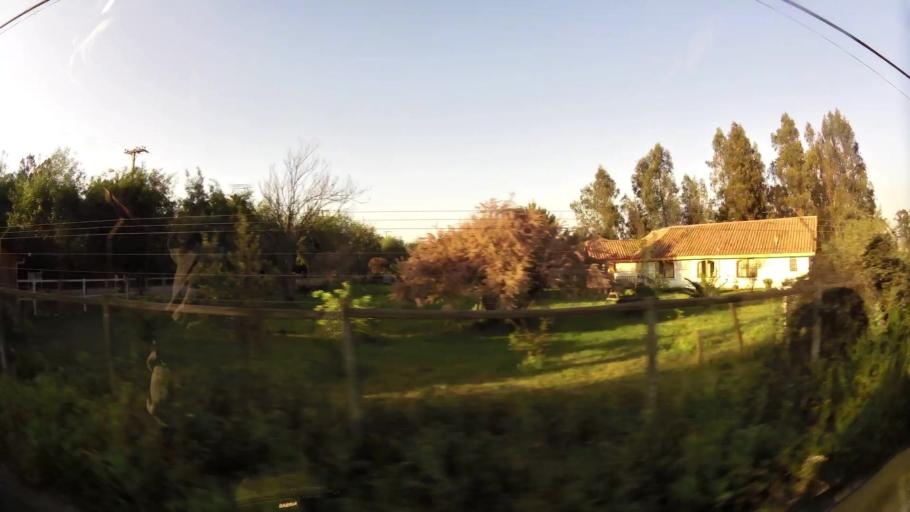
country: CL
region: Santiago Metropolitan
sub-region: Provincia de Talagante
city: Penaflor
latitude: -33.5931
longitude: -70.8571
